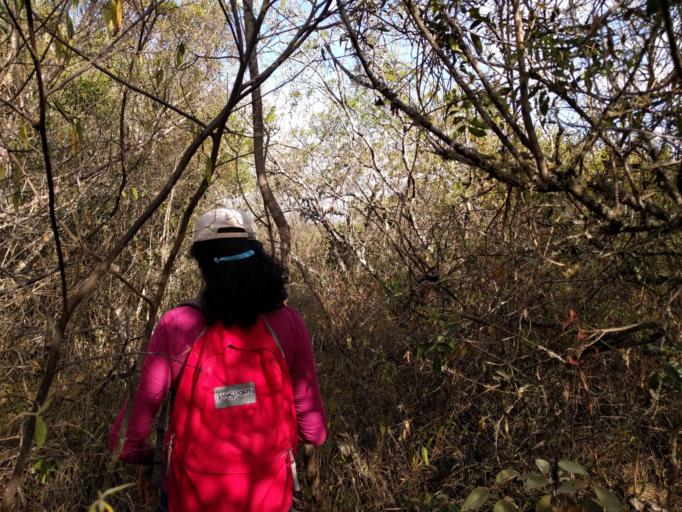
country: BO
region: Santa Cruz
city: Samaipata
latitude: -18.1875
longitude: -63.8904
